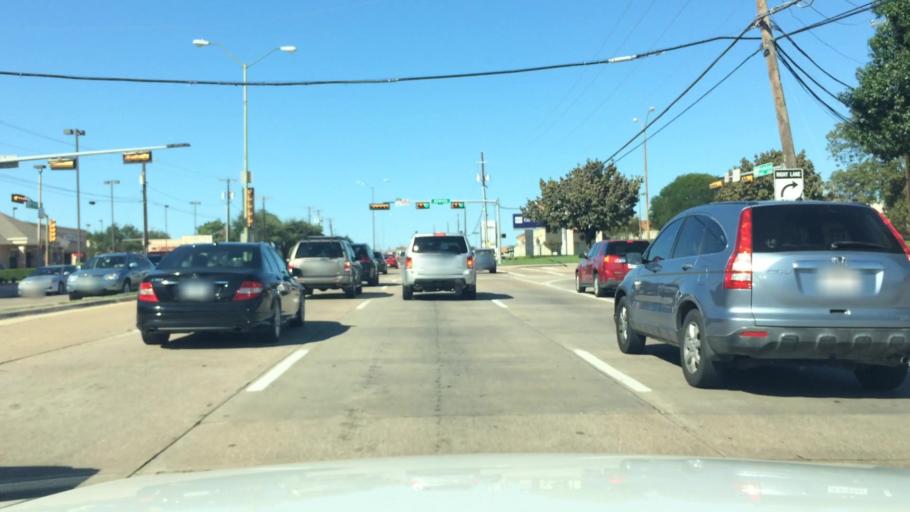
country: US
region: Texas
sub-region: Dallas County
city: Addison
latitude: 32.9493
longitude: -96.8035
